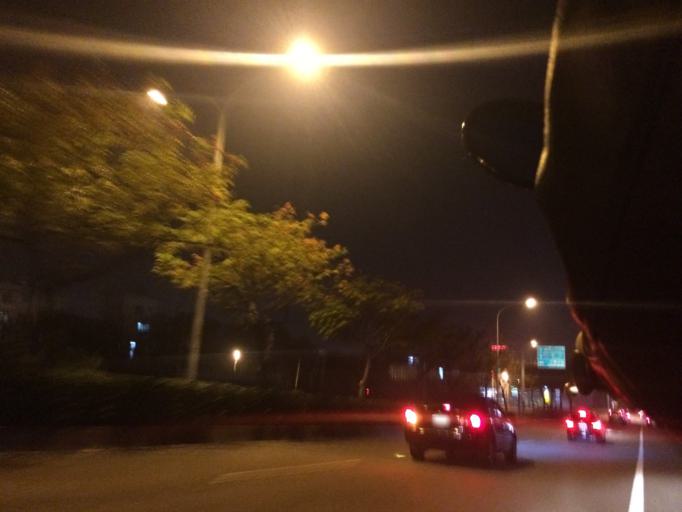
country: TW
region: Taiwan
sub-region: Hsinchu
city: Hsinchu
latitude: 24.7004
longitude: 120.8853
